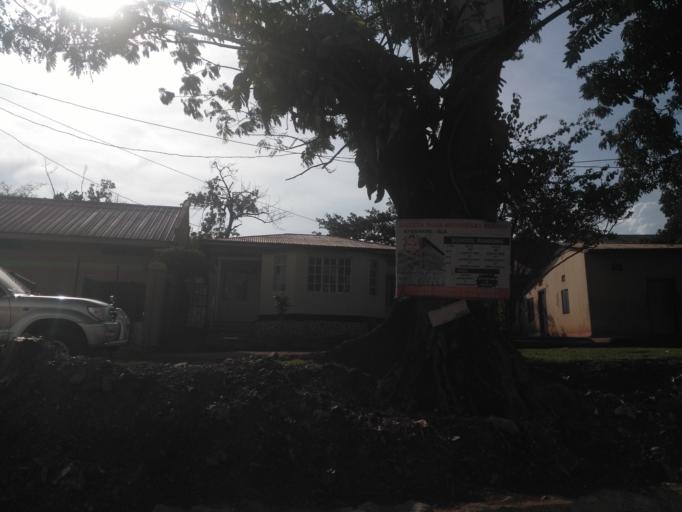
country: UG
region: Central Region
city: Kampala Central Division
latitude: 0.3621
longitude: 32.5698
